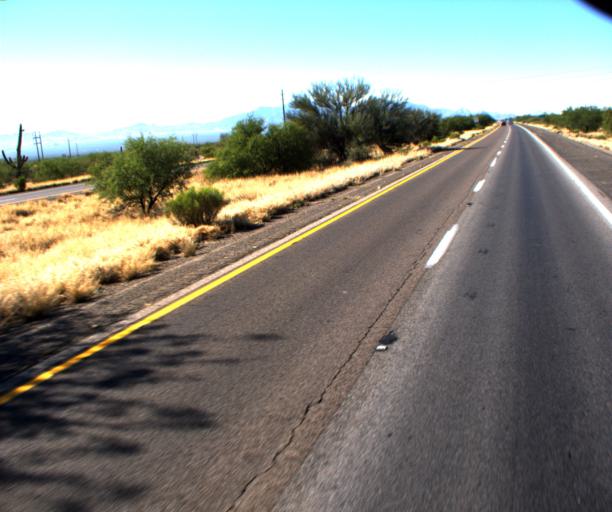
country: US
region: Arizona
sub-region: Pima County
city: Sahuarita
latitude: 31.9883
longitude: -110.9920
